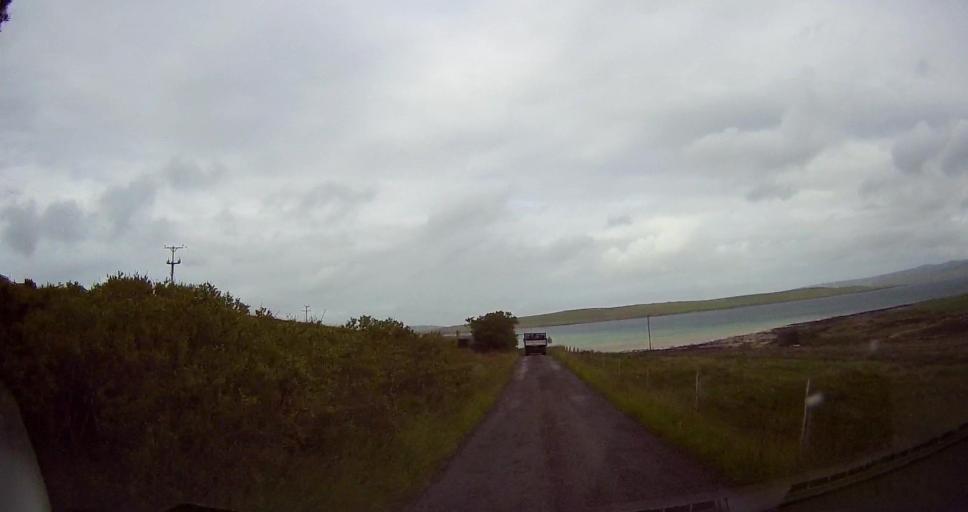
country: GB
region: Scotland
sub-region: Orkney Islands
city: Stromness
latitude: 58.9045
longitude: -3.3170
